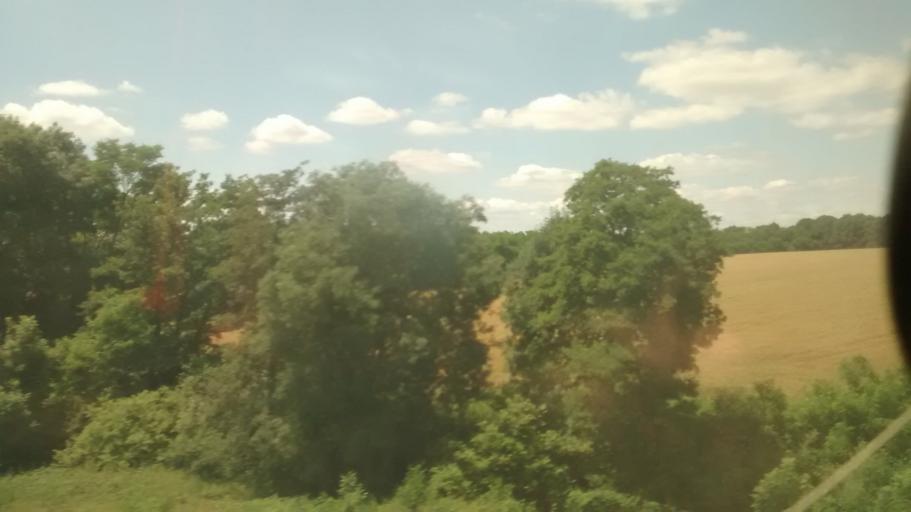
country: FR
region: Rhone-Alpes
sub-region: Departement de l'Ain
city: Civrieux
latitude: 45.9523
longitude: 4.8654
